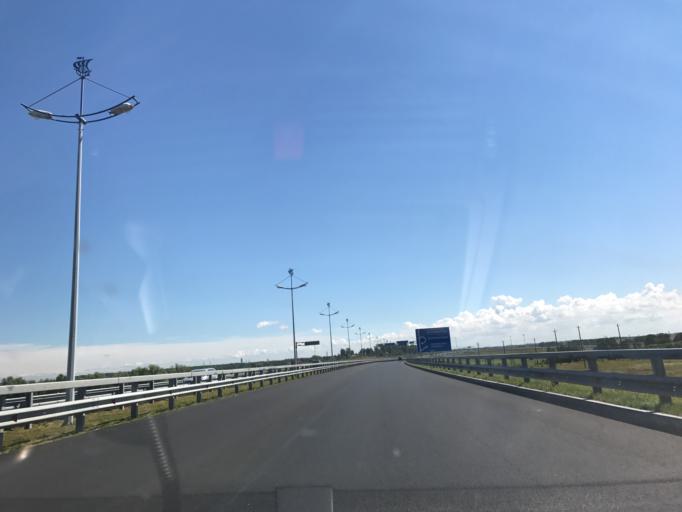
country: RU
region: Kaliningrad
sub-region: Zelenogradskiy Rayon
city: Zelenogradsk
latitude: 54.9152
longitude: 20.4863
